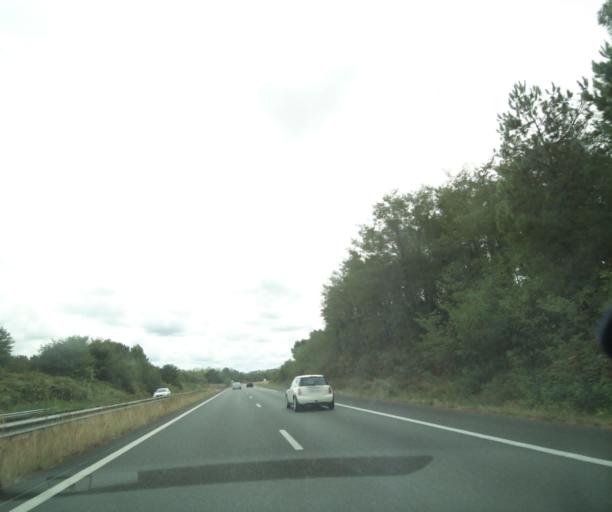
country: FR
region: Aquitaine
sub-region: Departement de la Gironde
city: Reignac
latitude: 45.2266
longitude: -0.5180
